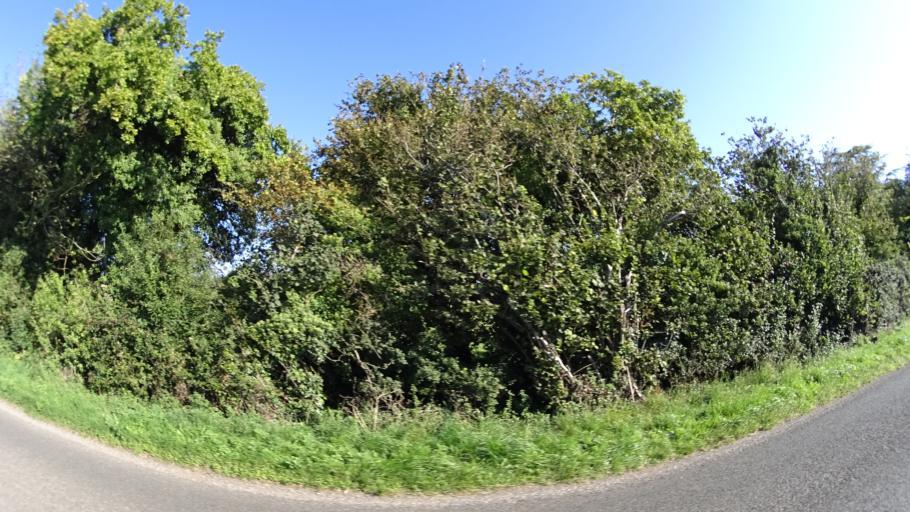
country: GB
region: England
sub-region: Hampshire
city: Abbotts Ann
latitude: 51.1620
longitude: -1.5794
